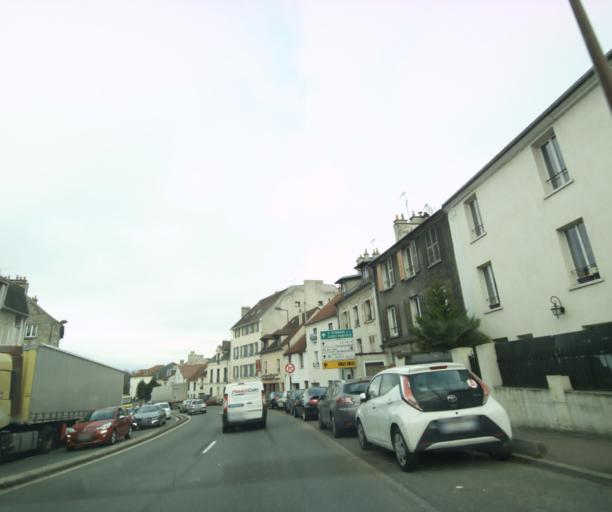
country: FR
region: Ile-de-France
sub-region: Departement des Yvelines
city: Le Port-Marly
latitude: 48.8783
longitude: 2.1079
